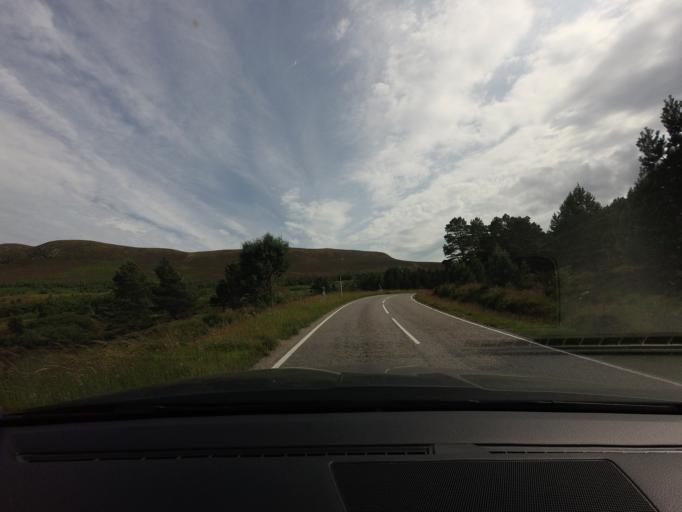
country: GB
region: Scotland
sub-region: Highland
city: Alness
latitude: 57.8398
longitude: -4.2690
